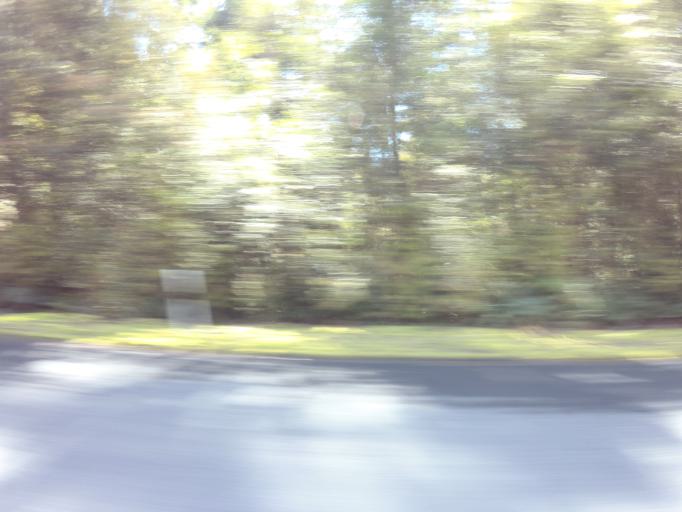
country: AU
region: Tasmania
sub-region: Huon Valley
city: Geeveston
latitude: -42.8190
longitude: 146.2842
